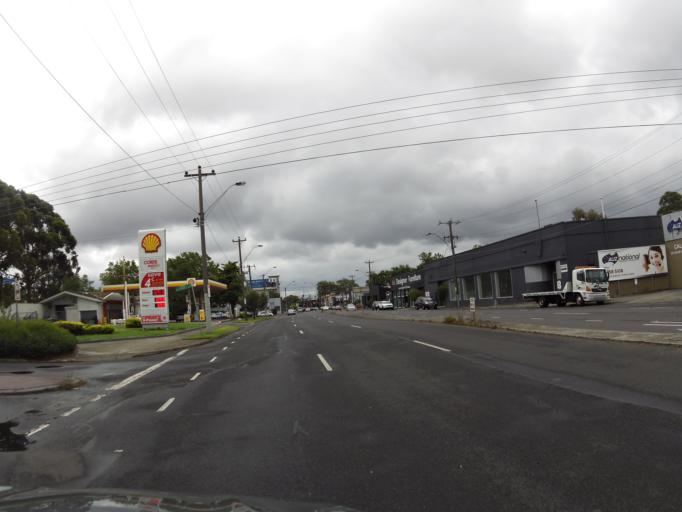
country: AU
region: Victoria
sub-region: Darebin
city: Fairfield
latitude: -37.7837
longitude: 145.0149
